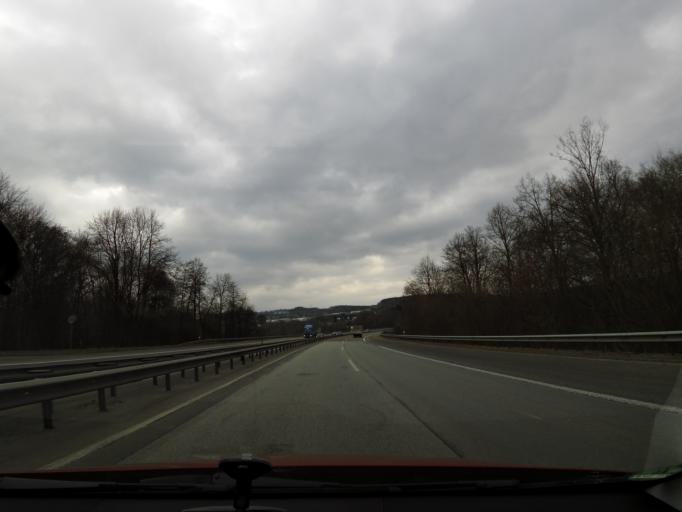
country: DE
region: Rheinland-Pfalz
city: Hohr-Grenzhausen
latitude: 50.4467
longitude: 7.6725
